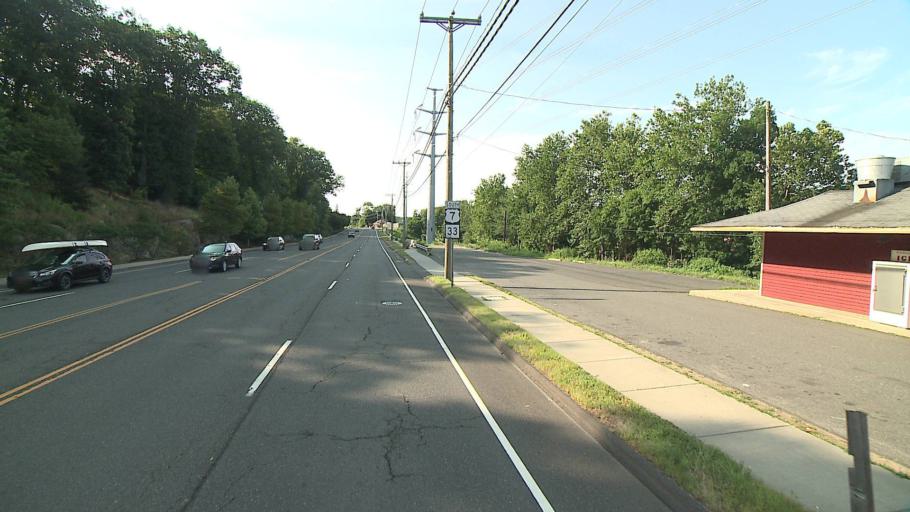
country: US
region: Connecticut
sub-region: Fairfield County
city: Wilton
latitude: 41.1948
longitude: -73.4303
